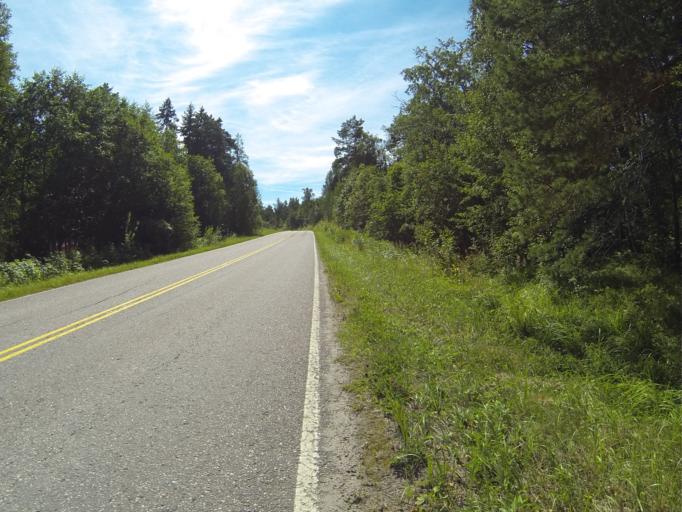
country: FI
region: Varsinais-Suomi
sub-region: Salo
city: Halikko
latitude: 60.2752
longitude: 22.9837
